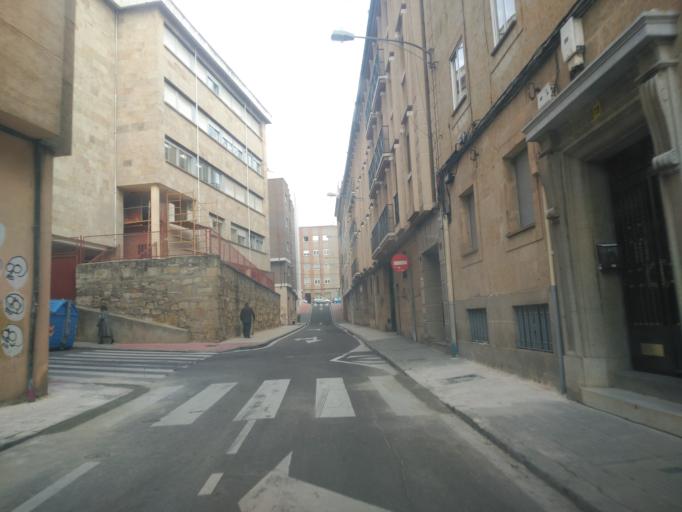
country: ES
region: Castille and Leon
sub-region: Provincia de Salamanca
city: Salamanca
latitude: 40.9622
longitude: -5.6577
